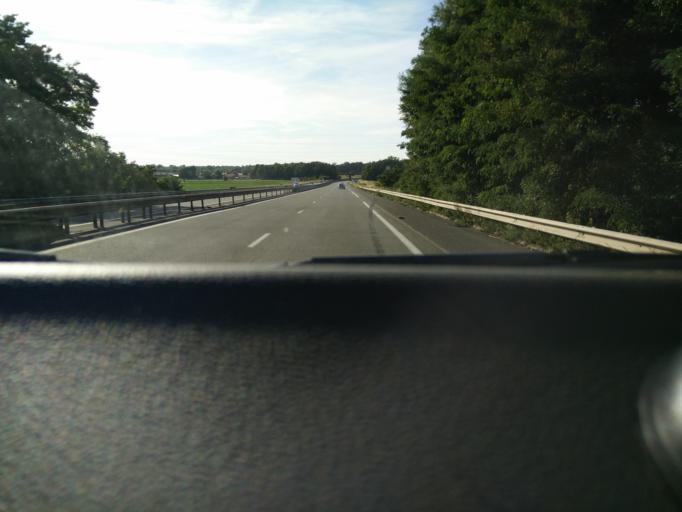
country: FR
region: Nord-Pas-de-Calais
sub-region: Departement du Nord
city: Escaudain
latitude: 50.3305
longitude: 3.3300
